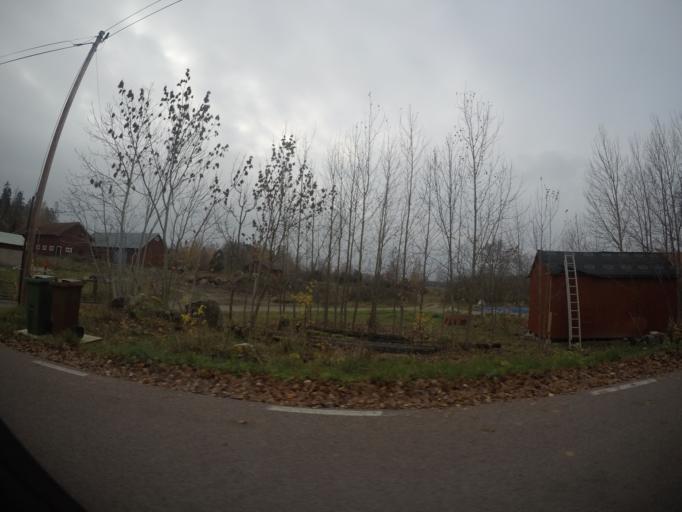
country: SE
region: Vaestmanland
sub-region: Vasteras
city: Vasteras
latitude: 59.6449
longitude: 16.4706
